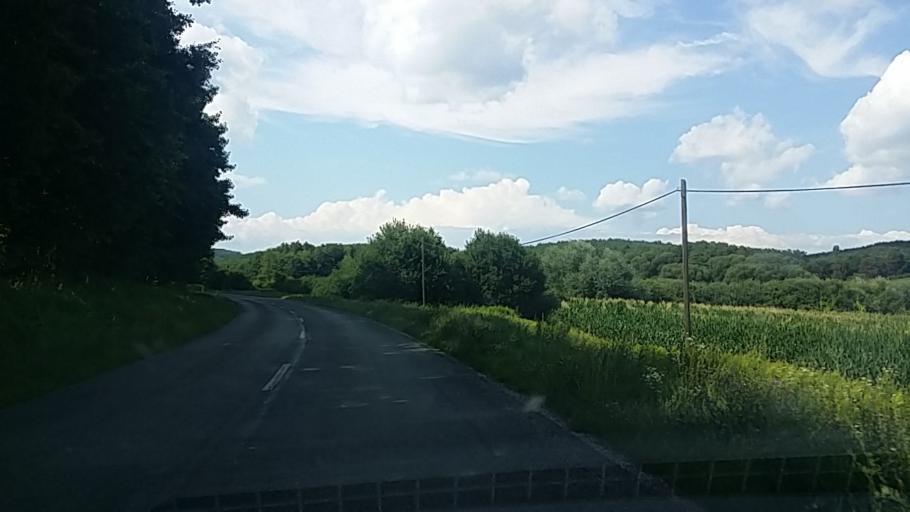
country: HU
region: Zala
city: Becsehely
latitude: 46.4564
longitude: 16.8111
